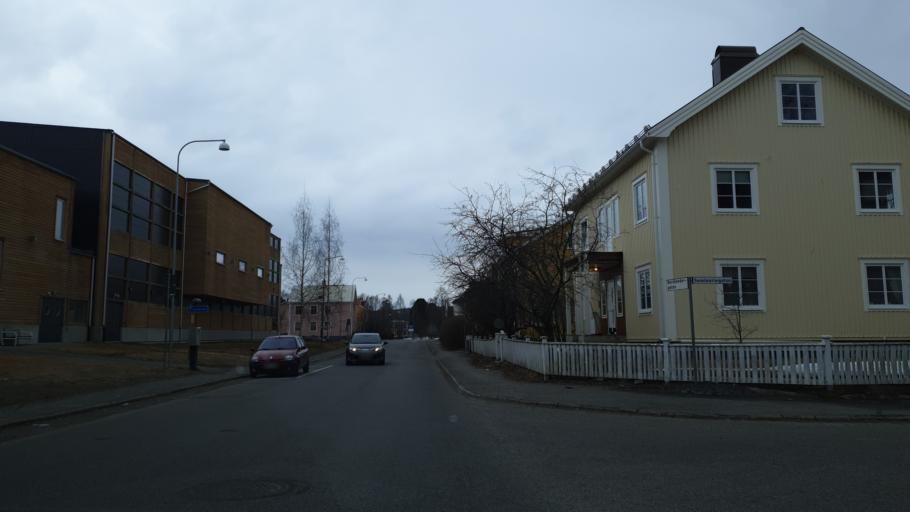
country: SE
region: Vaesterbotten
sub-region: Skelleftea Kommun
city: Skelleftea
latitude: 64.7527
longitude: 20.9405
